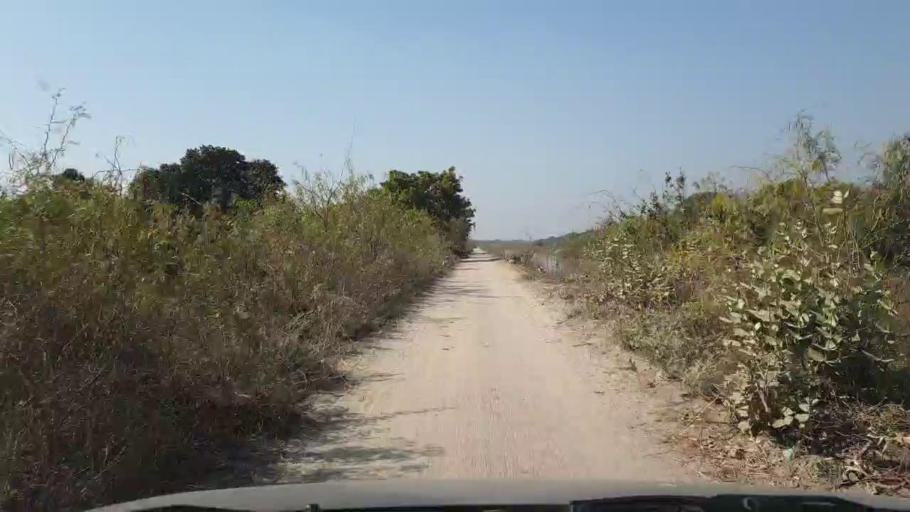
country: PK
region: Sindh
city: Tando Jam
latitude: 25.4486
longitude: 68.6201
